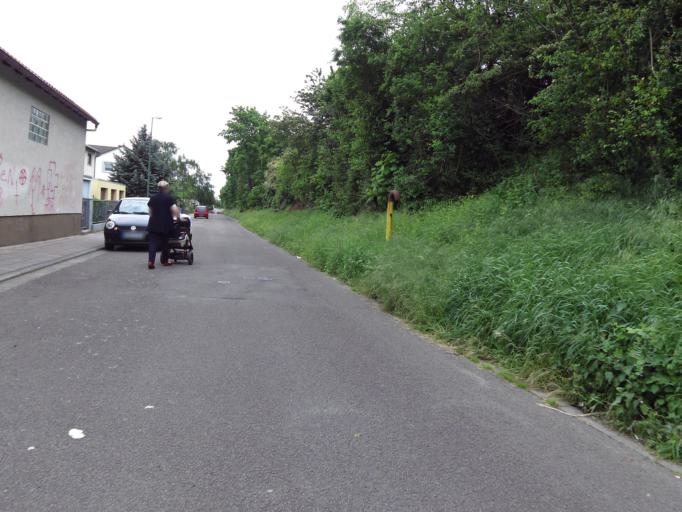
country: DE
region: Rheinland-Pfalz
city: Bad Duerkheim
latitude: 49.4652
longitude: 8.1913
